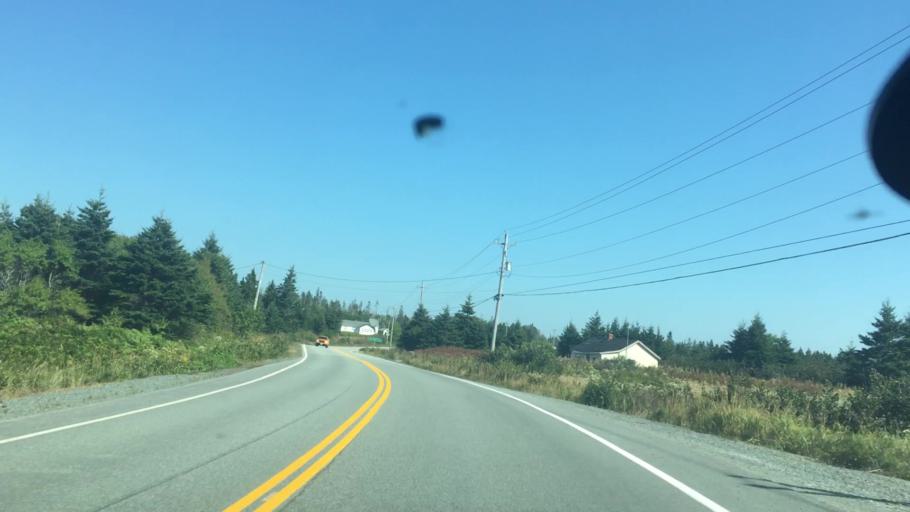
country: CA
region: Nova Scotia
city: New Glasgow
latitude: 44.9188
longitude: -62.3054
